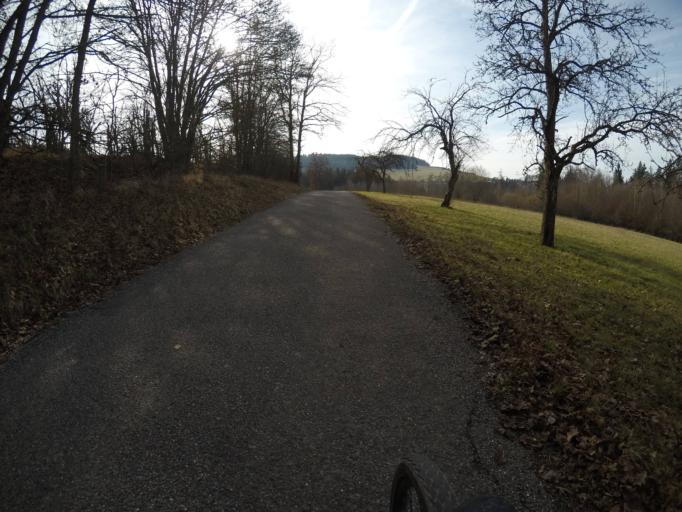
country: DE
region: Baden-Wuerttemberg
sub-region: Karlsruhe Region
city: Wildberg
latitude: 48.6368
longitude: 8.7664
